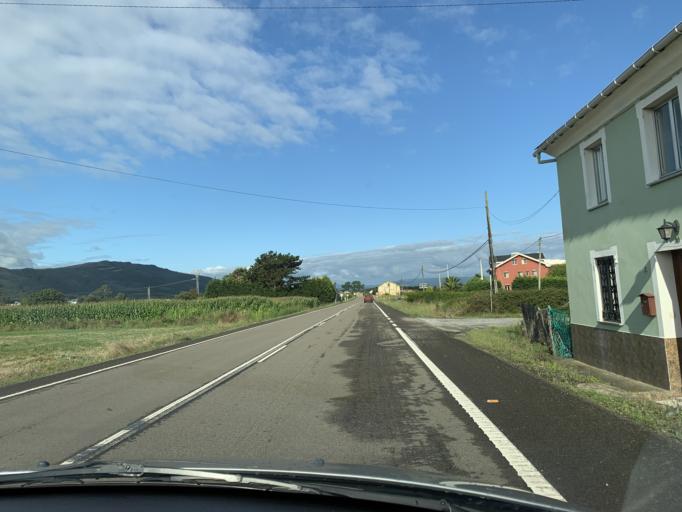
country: ES
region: Galicia
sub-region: Provincia de Lugo
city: Ribadeo
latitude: 43.5468
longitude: -7.1087
